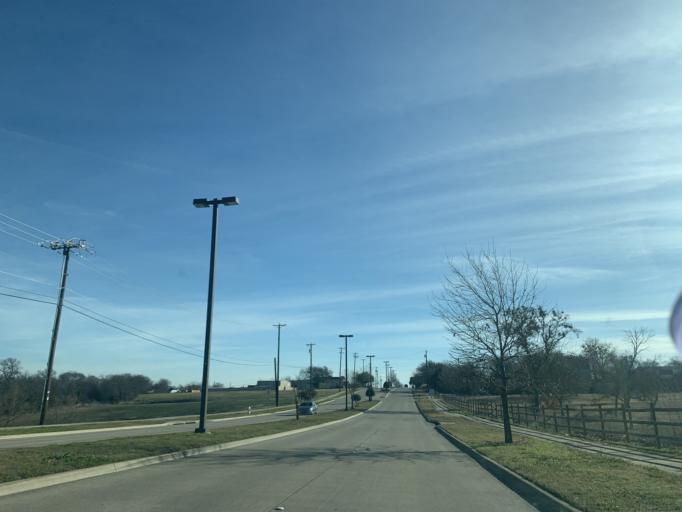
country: US
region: Texas
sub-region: Dallas County
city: DeSoto
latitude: 32.5751
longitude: -96.8307
